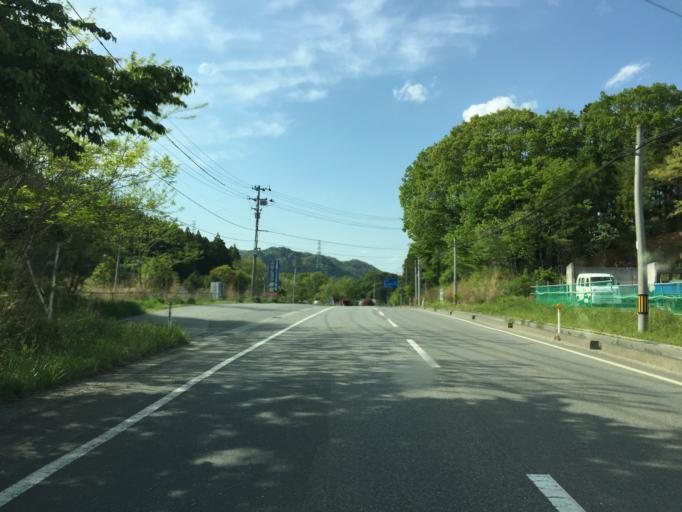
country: JP
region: Fukushima
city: Namie
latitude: 37.3780
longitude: 140.9580
